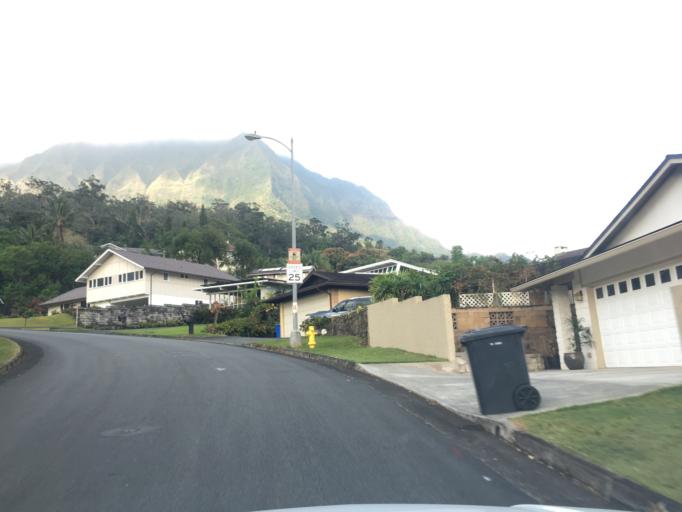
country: US
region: Hawaii
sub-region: Honolulu County
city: Maunawili
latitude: 21.3597
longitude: -157.7688
